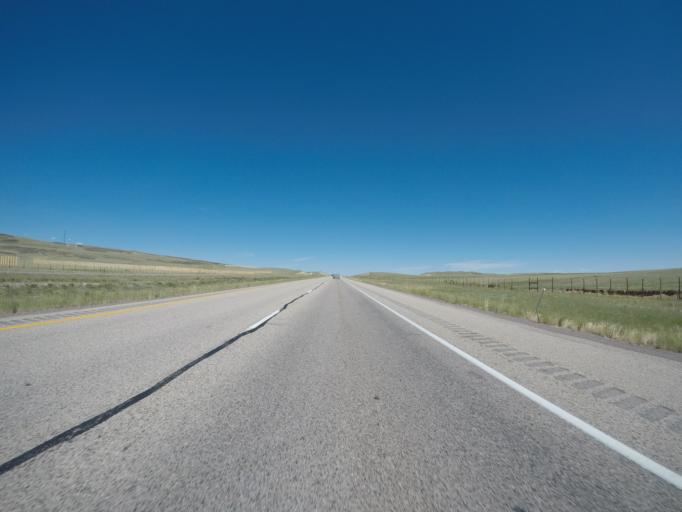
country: US
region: Wyoming
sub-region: Albany County
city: Laramie
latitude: 41.4901
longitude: -106.0349
